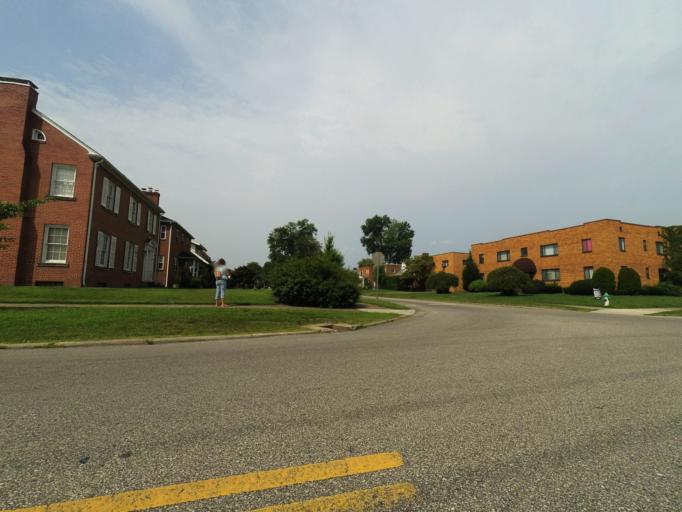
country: US
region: West Virginia
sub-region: Cabell County
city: Huntington
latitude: 38.4134
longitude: -82.4628
